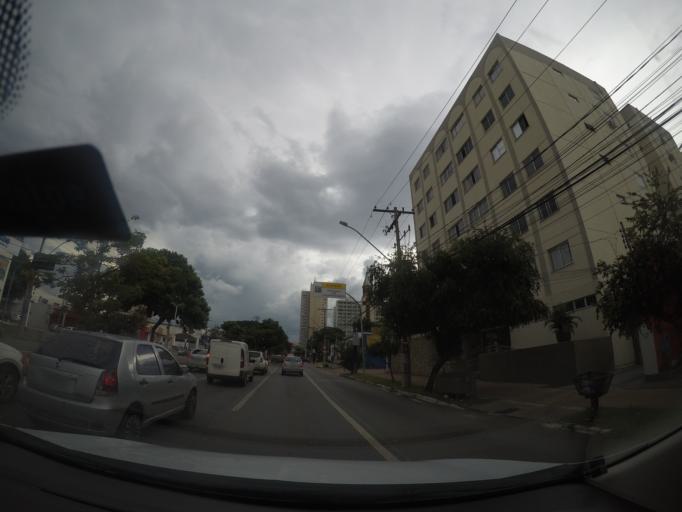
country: BR
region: Goias
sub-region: Goiania
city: Goiania
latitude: -16.6793
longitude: -49.2519
